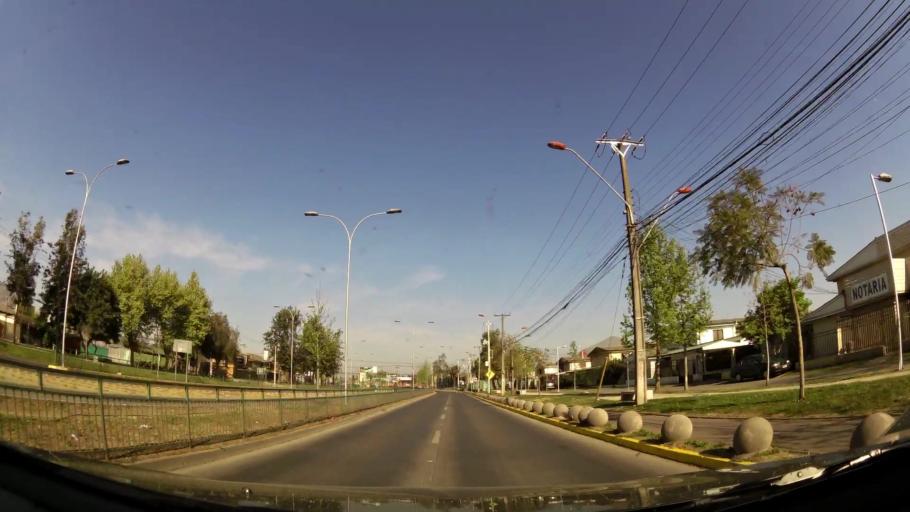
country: CL
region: Santiago Metropolitan
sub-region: Provincia de Santiago
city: Santiago
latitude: -33.3971
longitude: -70.6677
